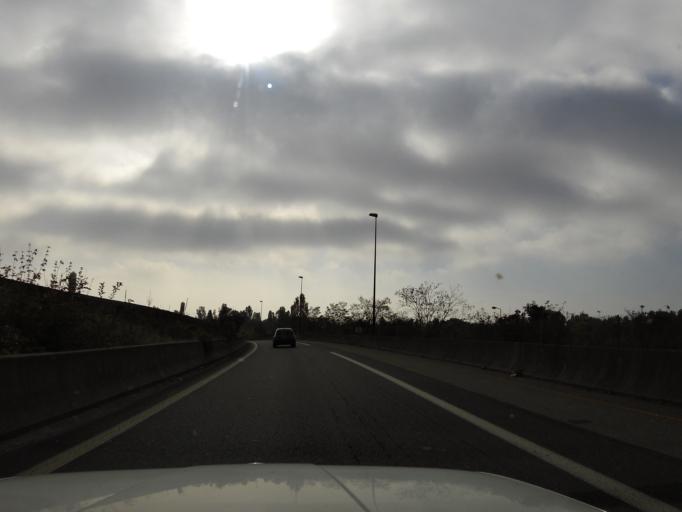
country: FR
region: Rhone-Alpes
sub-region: Departement du Rhone
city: Vaulx-en-Velin
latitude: 45.7977
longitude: 4.9264
